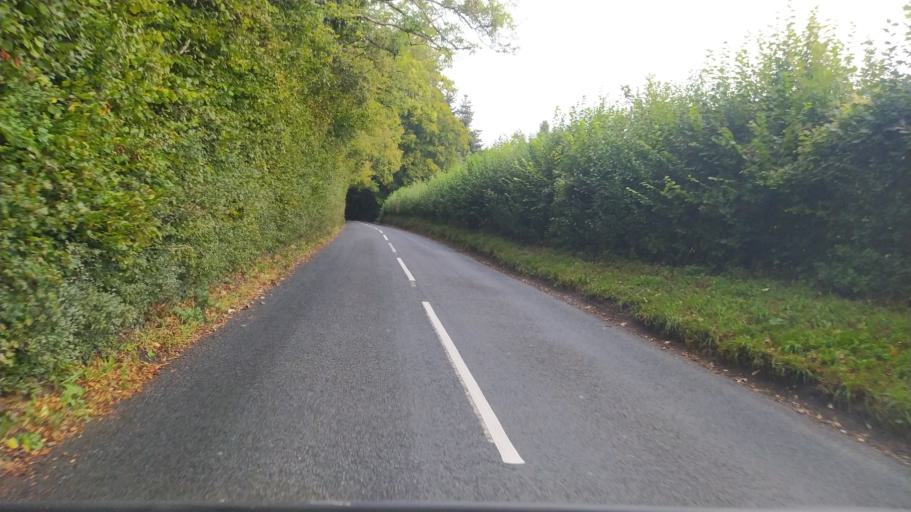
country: GB
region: England
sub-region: Hampshire
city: East Dean
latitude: 51.0681
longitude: -1.5521
